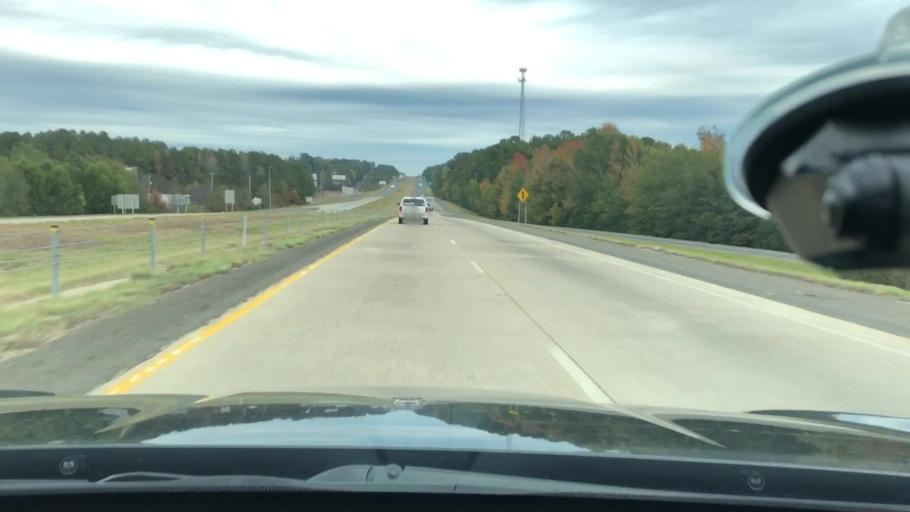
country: US
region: Arkansas
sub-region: Clark County
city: Arkadelphia
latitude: 34.1857
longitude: -93.0696
